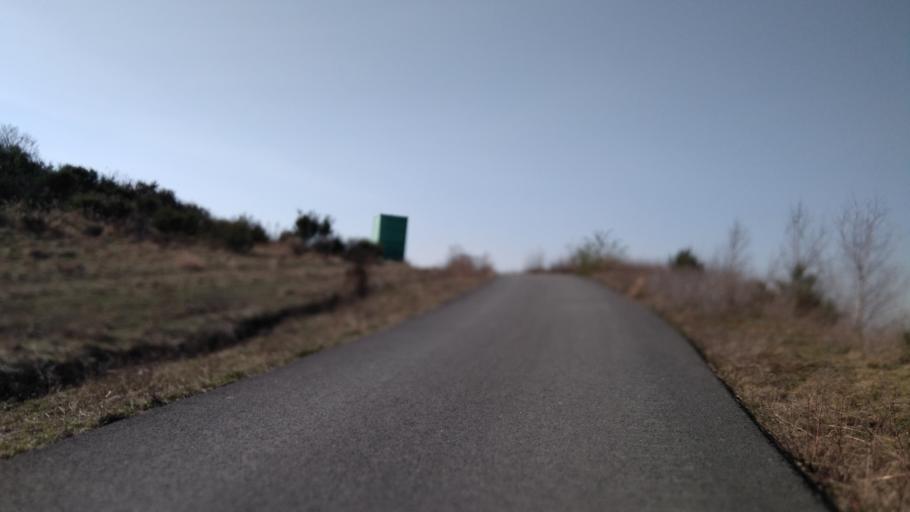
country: DE
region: North Rhine-Westphalia
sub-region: Regierungsbezirk Munster
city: Bottrop
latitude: 51.5552
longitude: 6.8784
